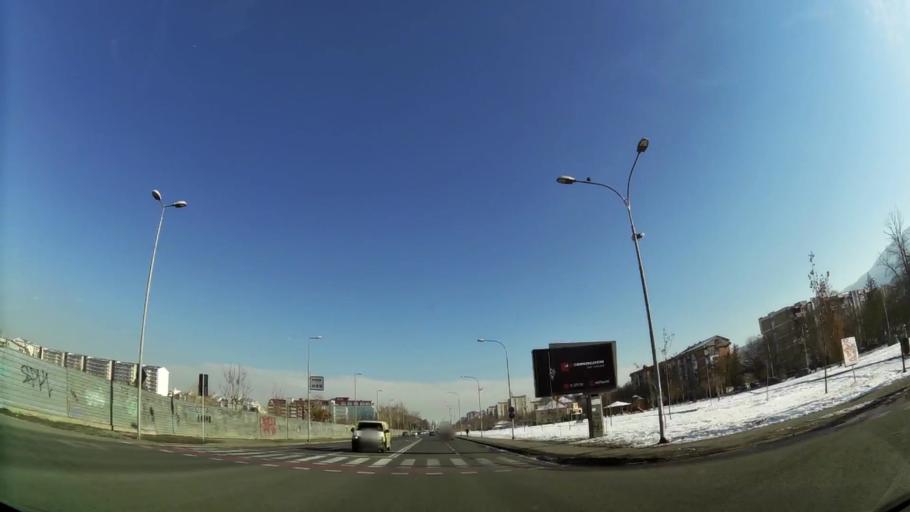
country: MK
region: Karpos
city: Skopje
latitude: 41.9970
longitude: 21.3995
